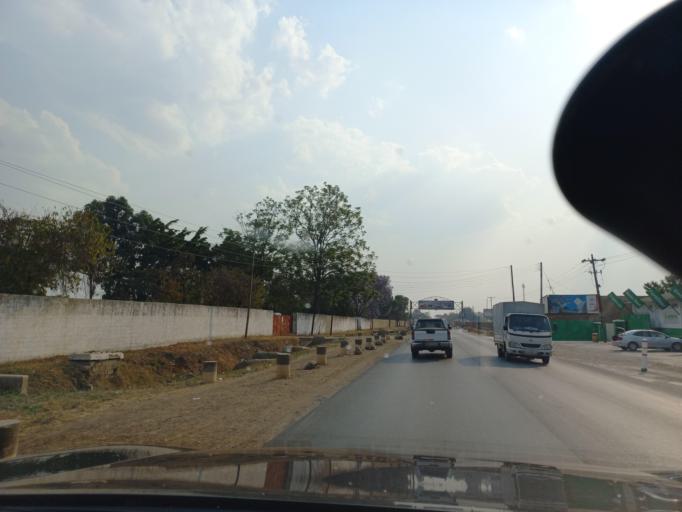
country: ZM
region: Lusaka
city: Lusaka
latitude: -15.4568
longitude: 28.2619
